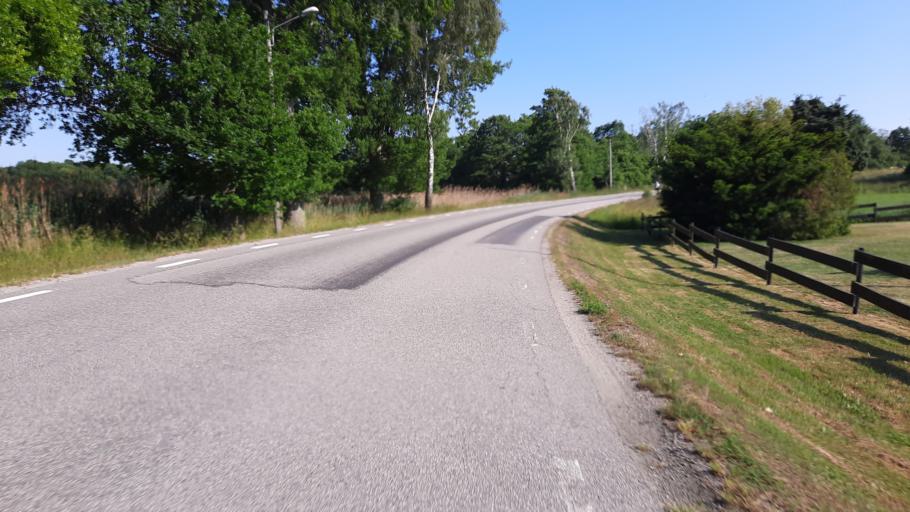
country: SE
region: Blekinge
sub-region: Karlskrona Kommun
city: Sturko
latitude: 56.0979
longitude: 15.6950
